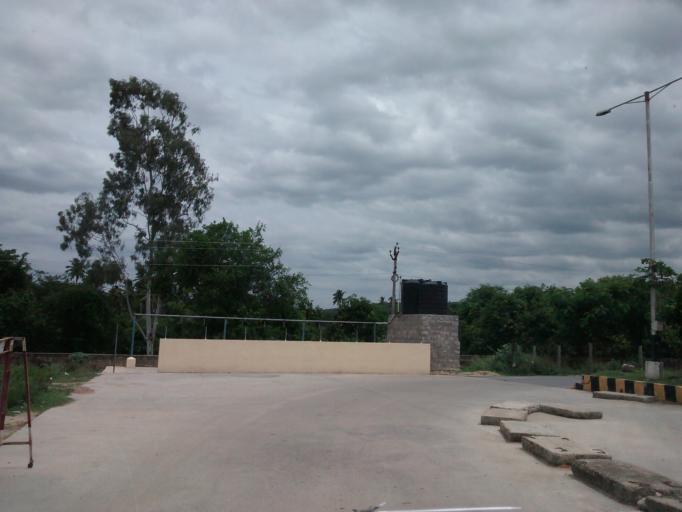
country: IN
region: Andhra Pradesh
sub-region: Chittoor
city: Chittoor
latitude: 13.2760
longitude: 79.0394
